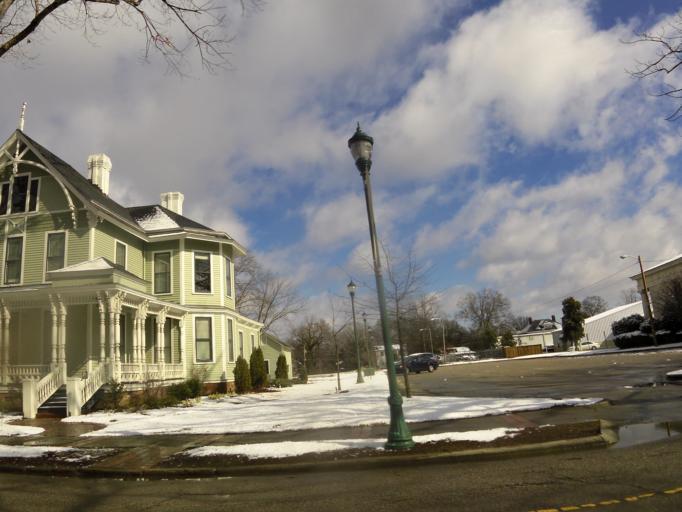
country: US
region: North Carolina
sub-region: Wilson County
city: Wilson
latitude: 35.7273
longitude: -77.9126
